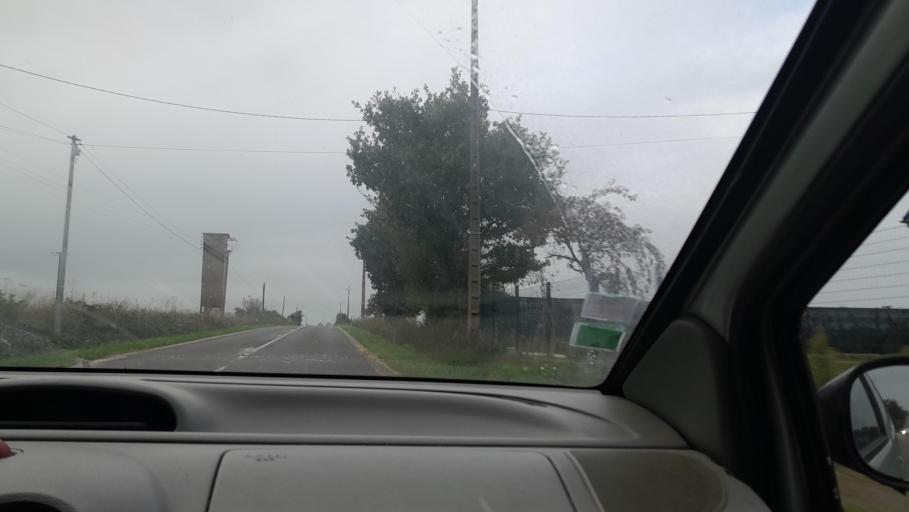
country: FR
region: Pays de la Loire
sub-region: Departement de la Mayenne
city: Congrier
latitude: 47.8142
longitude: -1.1474
